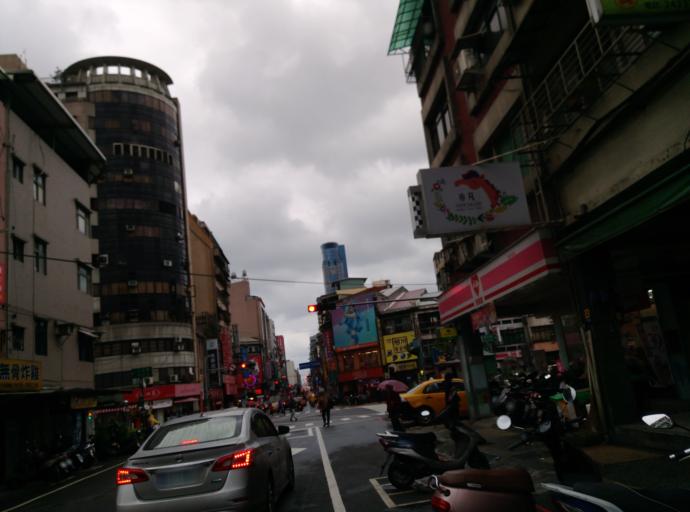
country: TW
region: Taiwan
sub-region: Keelung
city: Keelung
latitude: 25.1265
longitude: 121.7414
